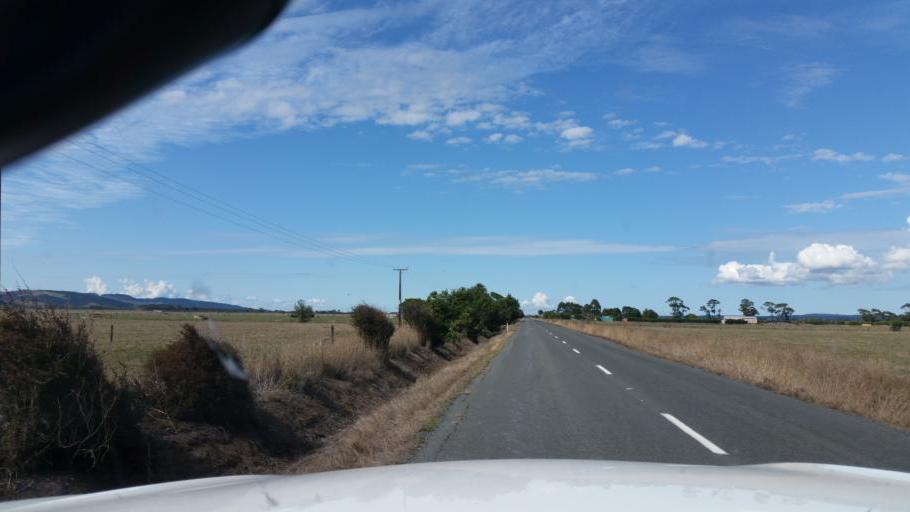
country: NZ
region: Northland
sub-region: Kaipara District
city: Dargaville
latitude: -36.1266
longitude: 174.0523
